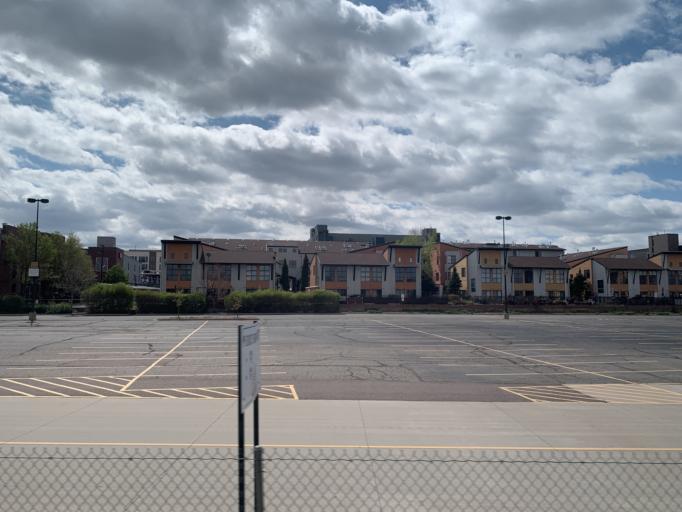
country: US
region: Colorado
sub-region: Denver County
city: Denver
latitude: 39.7665
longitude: -104.9808
